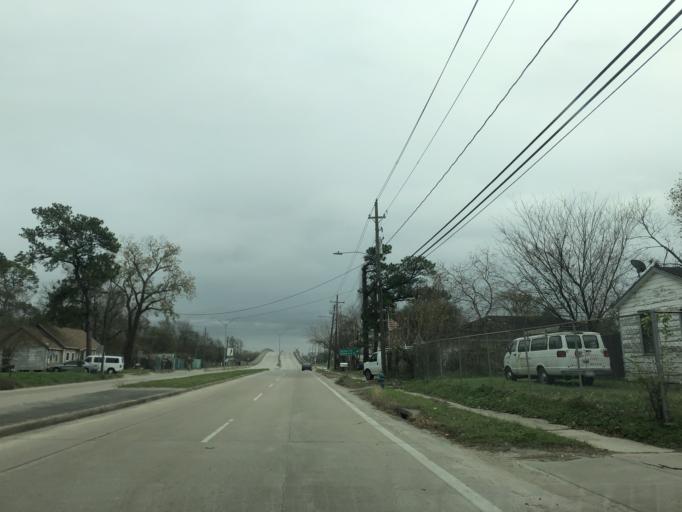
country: US
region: Texas
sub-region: Harris County
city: Jacinto City
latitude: 29.8313
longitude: -95.2933
